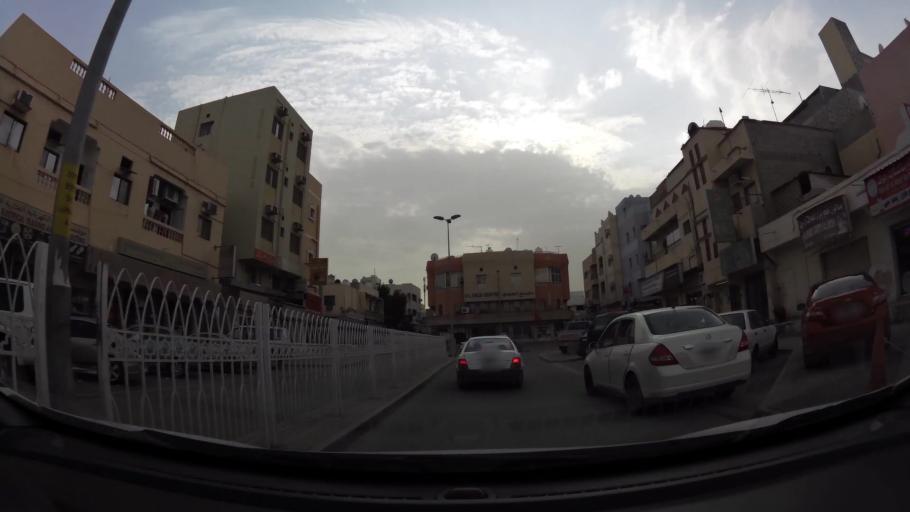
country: BH
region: Northern
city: Ar Rifa'
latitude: 26.1204
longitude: 50.5686
